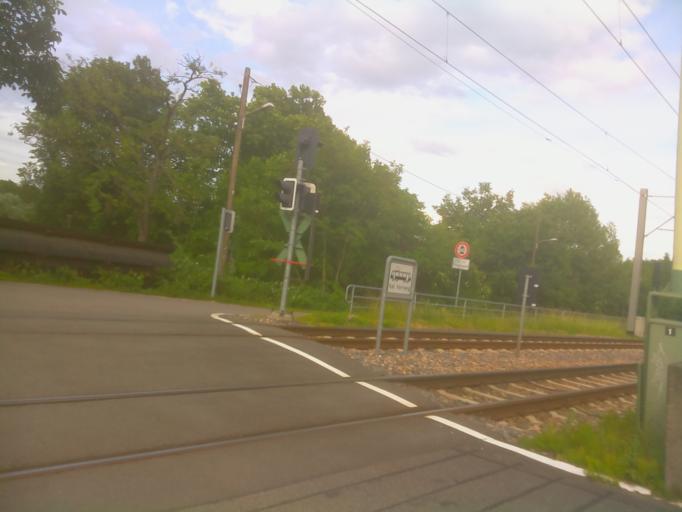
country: DE
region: Baden-Wuerttemberg
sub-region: Karlsruhe Region
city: Ilvesheim
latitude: 49.4763
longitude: 8.5277
